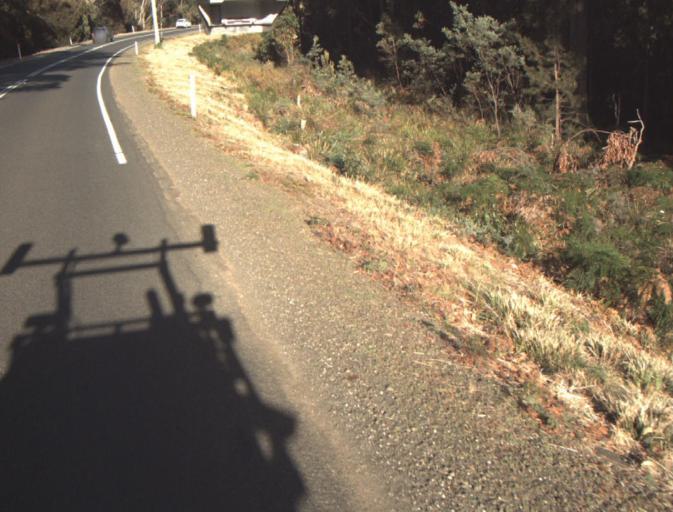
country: AU
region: Tasmania
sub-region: Launceston
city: Mayfield
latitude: -41.3380
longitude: 147.1629
